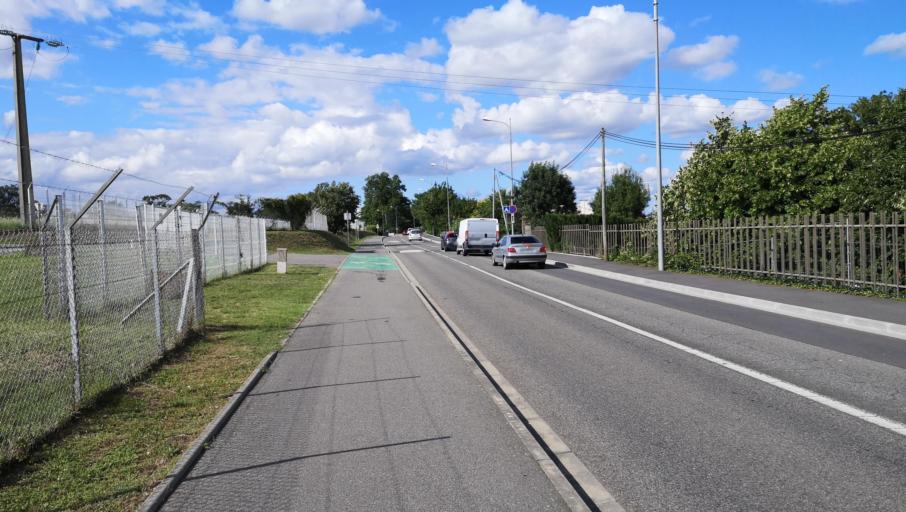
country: FR
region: Midi-Pyrenees
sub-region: Departement de la Haute-Garonne
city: Blagnac
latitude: 43.6168
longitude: 1.3880
